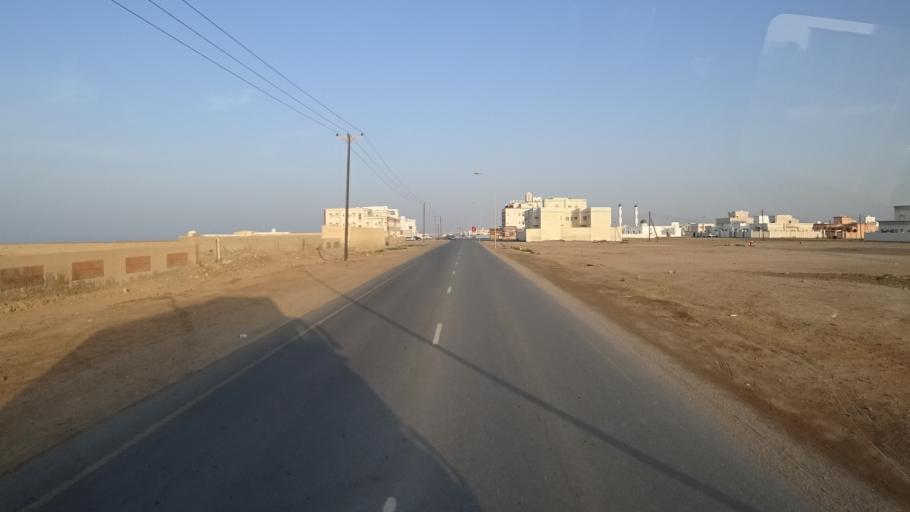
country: OM
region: Ash Sharqiyah
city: Sur
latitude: 22.6068
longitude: 59.4754
